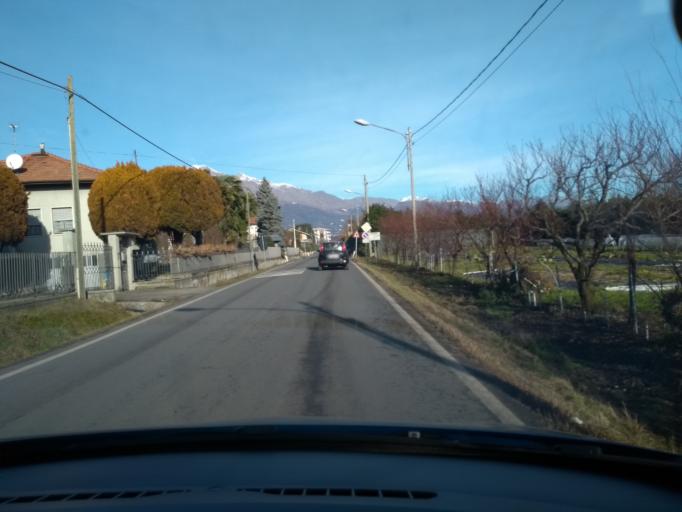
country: IT
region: Piedmont
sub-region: Provincia di Torino
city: Valperga
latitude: 45.3654
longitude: 7.6595
